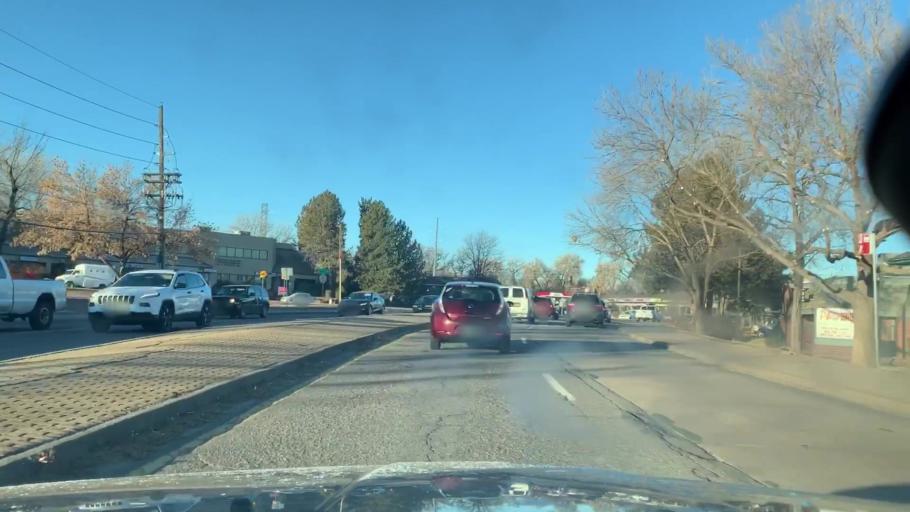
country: US
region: Colorado
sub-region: Arapahoe County
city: Glendale
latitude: 39.6750
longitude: -104.9005
